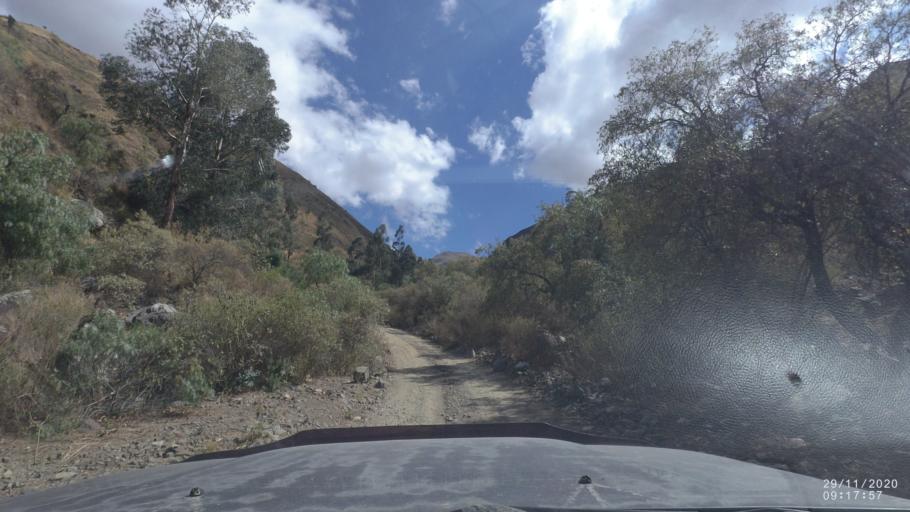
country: BO
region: Cochabamba
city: Cochabamba
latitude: -17.3227
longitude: -66.1832
